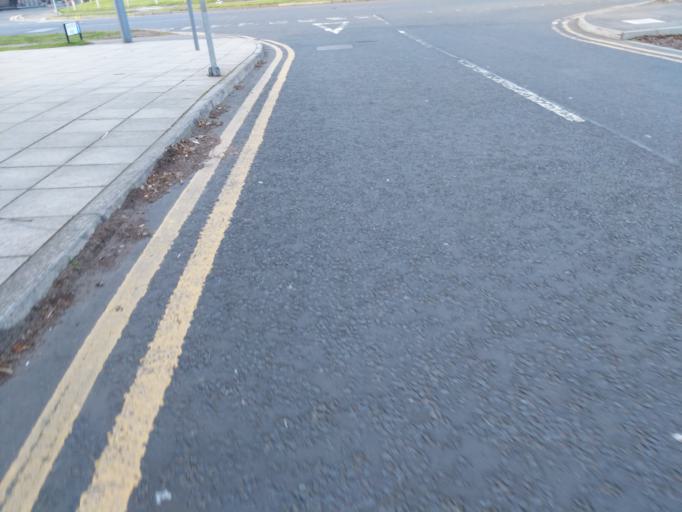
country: GB
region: Scotland
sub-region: Edinburgh
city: Currie
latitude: 55.9299
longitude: -3.2982
